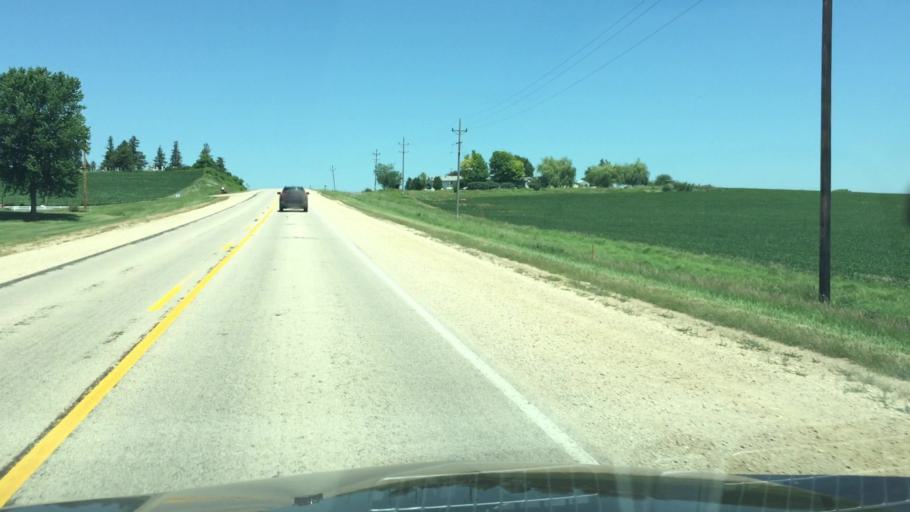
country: US
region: Iowa
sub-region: Cedar County
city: Mechanicsville
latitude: 41.9802
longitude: -91.1417
